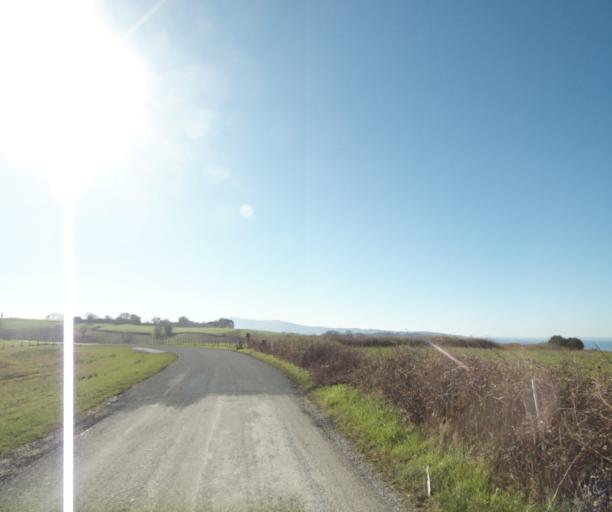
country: FR
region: Aquitaine
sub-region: Departement des Pyrenees-Atlantiques
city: Urrugne
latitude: 43.3742
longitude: -1.7212
